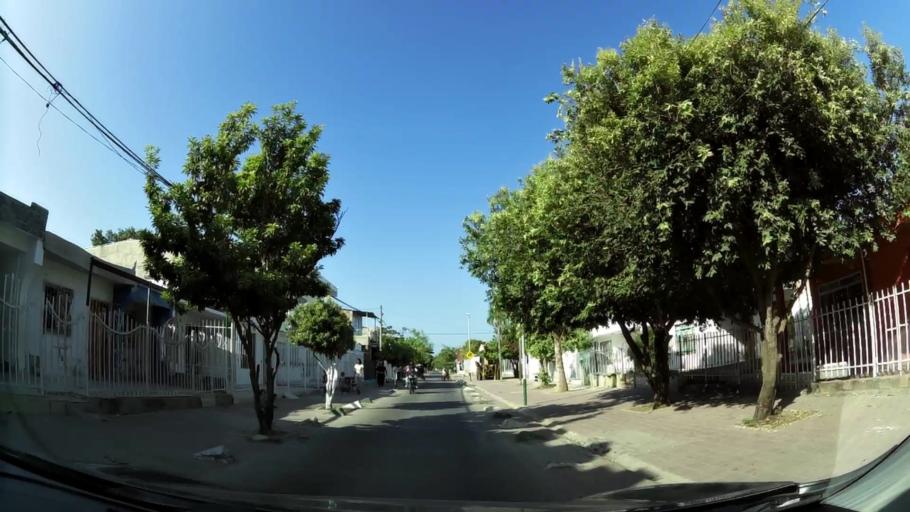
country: CO
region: Bolivar
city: Cartagena
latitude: 10.4086
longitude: -75.4966
